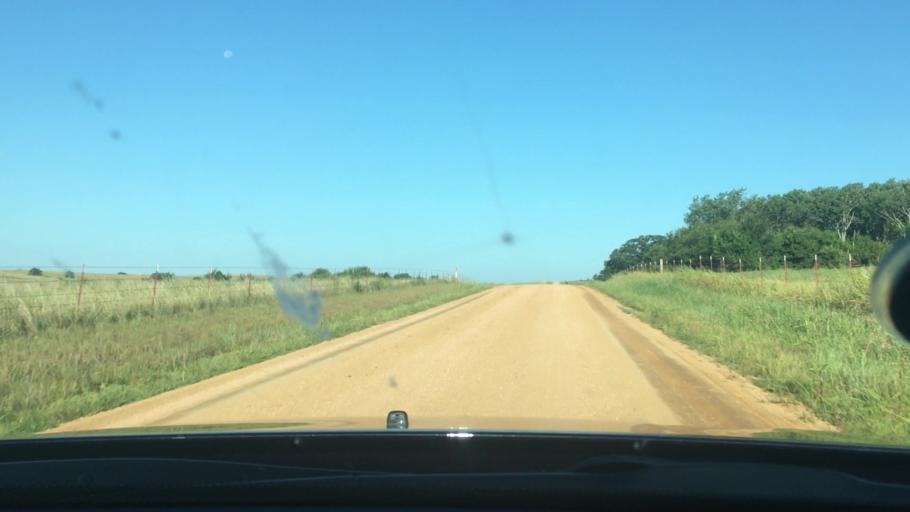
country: US
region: Oklahoma
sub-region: Johnston County
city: Tishomingo
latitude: 34.4194
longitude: -96.7659
